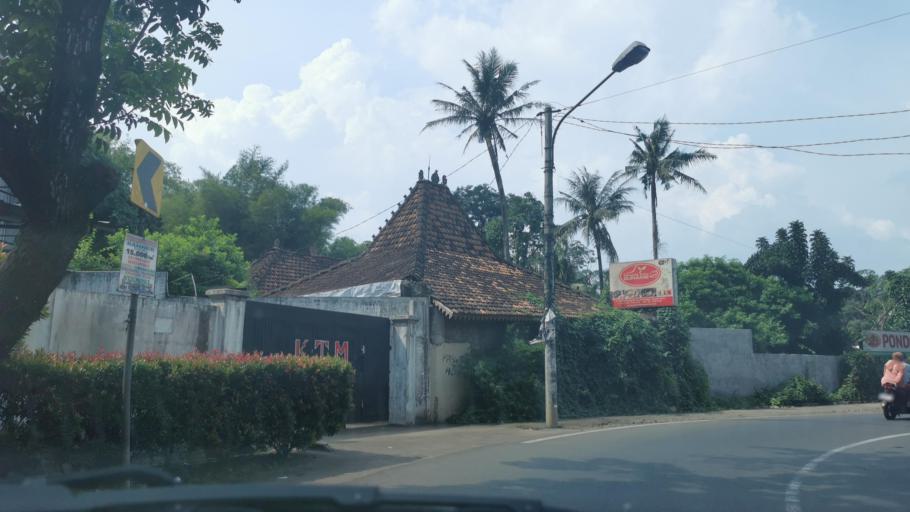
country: ID
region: West Java
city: Depok
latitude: -6.4080
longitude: 106.8331
